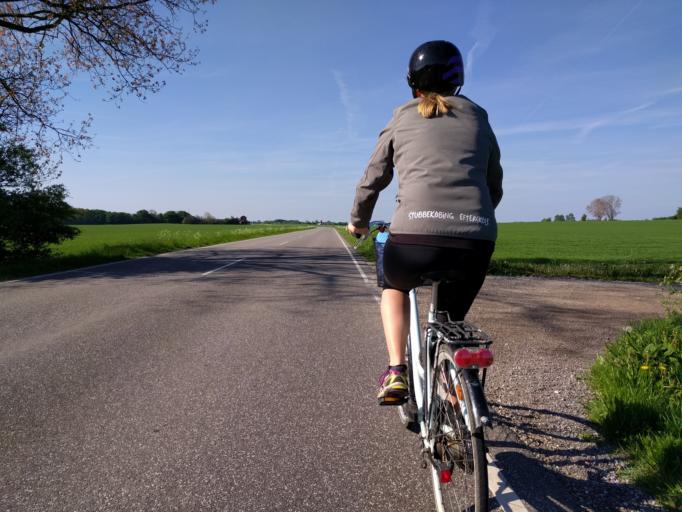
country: DK
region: Zealand
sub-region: Guldborgsund Kommune
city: Stubbekobing
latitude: 54.7885
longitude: 11.9882
